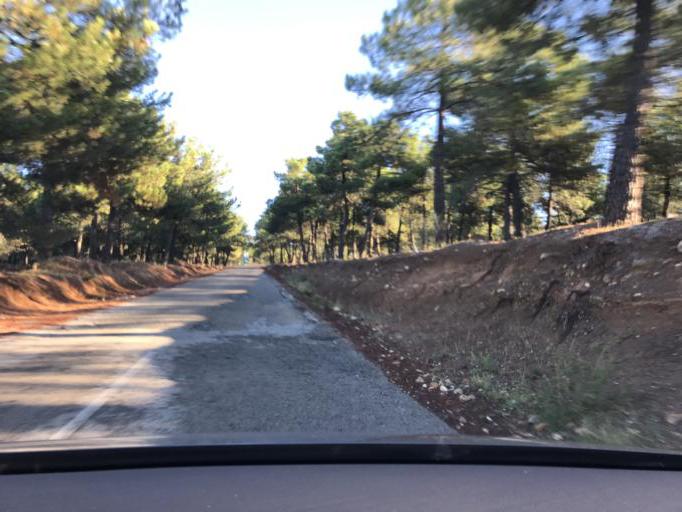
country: ES
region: Andalusia
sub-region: Provincia de Granada
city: Viznar
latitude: 37.2256
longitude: -3.5381
